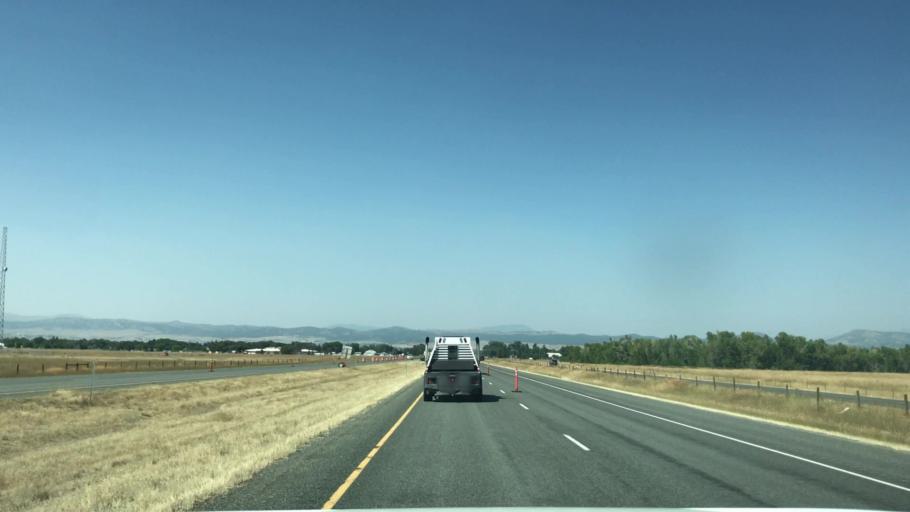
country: US
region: Montana
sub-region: Lewis and Clark County
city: Helena Valley West Central
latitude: 46.6507
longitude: -112.0112
